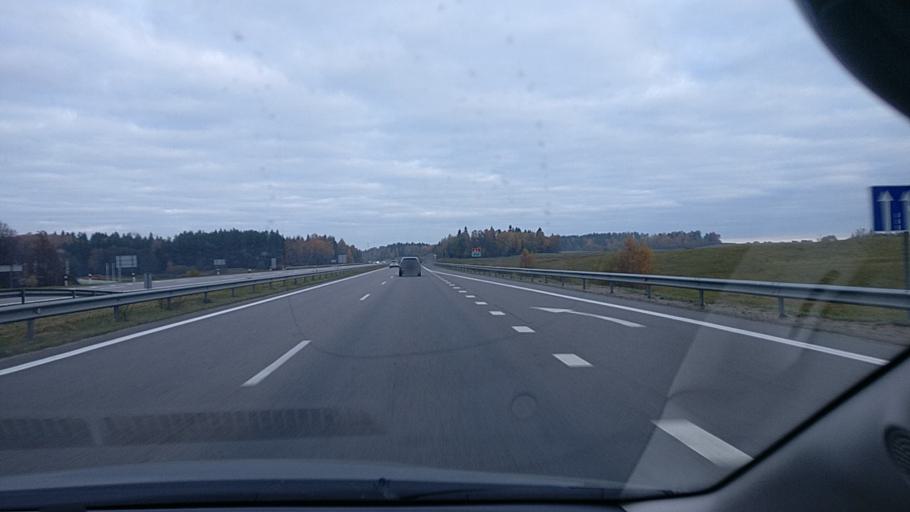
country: LT
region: Vilnius County
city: Pasilaiciai
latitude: 54.8055
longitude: 25.1585
